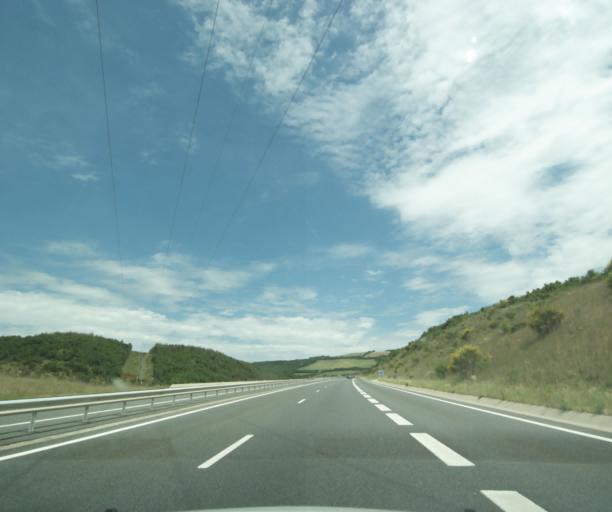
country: FR
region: Midi-Pyrenees
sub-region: Departement de l'Aveyron
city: Millau
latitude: 44.2098
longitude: 3.0686
